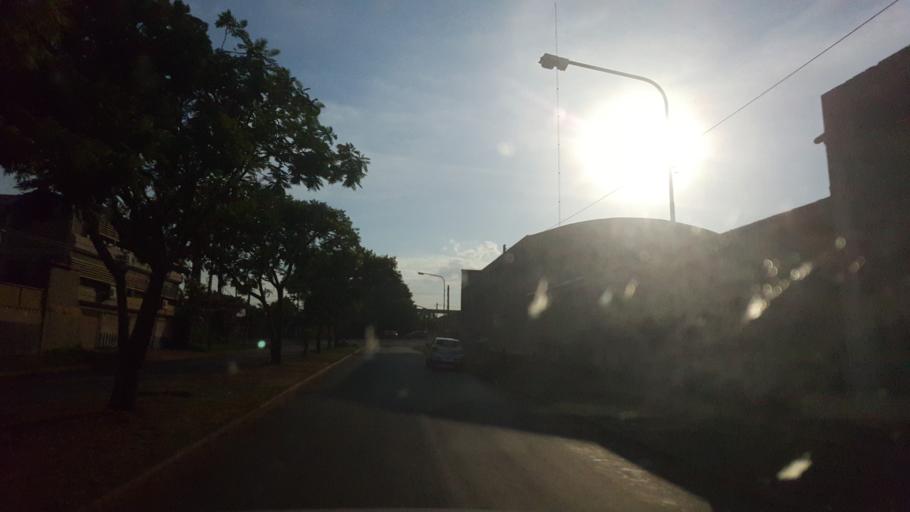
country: AR
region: Misiones
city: Garupa
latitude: -27.4372
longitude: -55.8816
